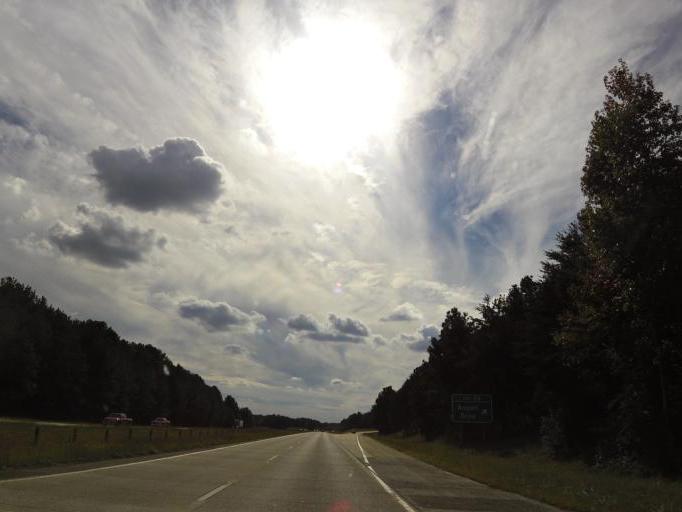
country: US
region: Georgia
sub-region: Cherokee County
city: Ball Ground
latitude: 34.3064
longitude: -84.4172
